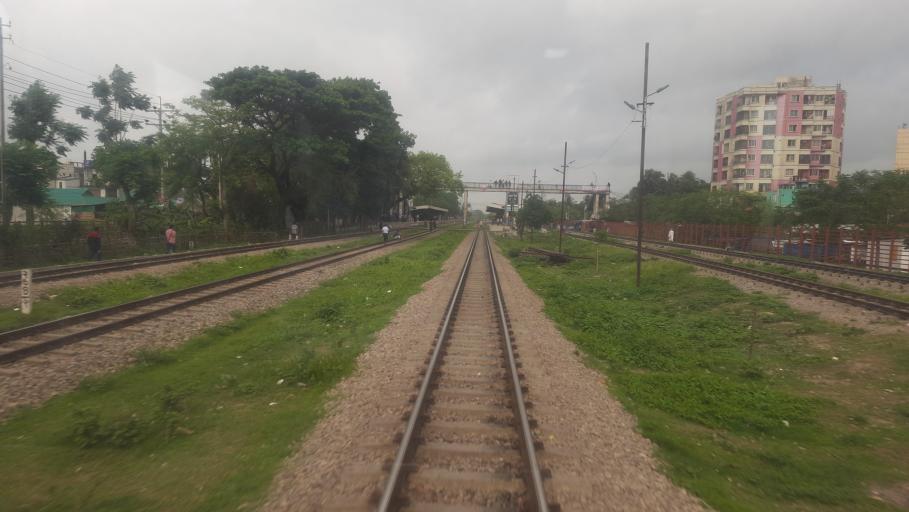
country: BD
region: Dhaka
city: Narsingdi
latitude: 23.9312
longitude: 90.7230
